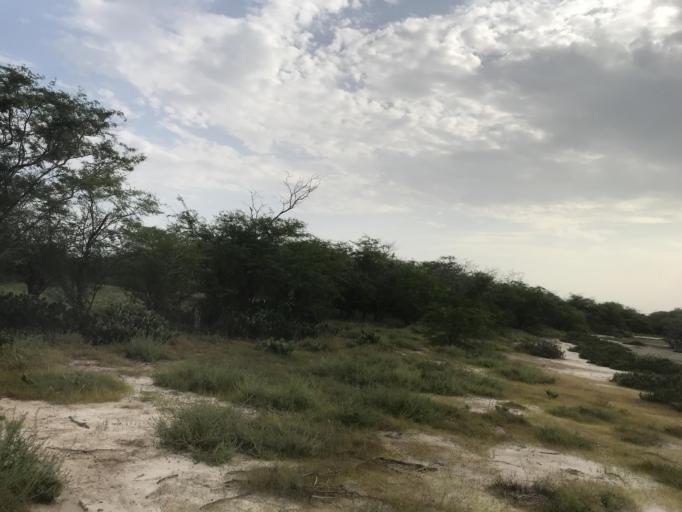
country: SN
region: Saint-Louis
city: Saint-Louis
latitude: 15.9278
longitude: -16.4662
